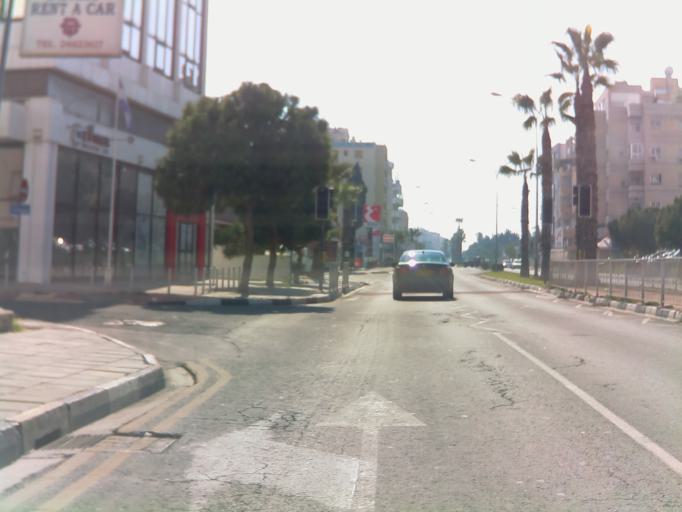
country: CY
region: Larnaka
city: Larnaca
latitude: 34.9103
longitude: 33.6293
